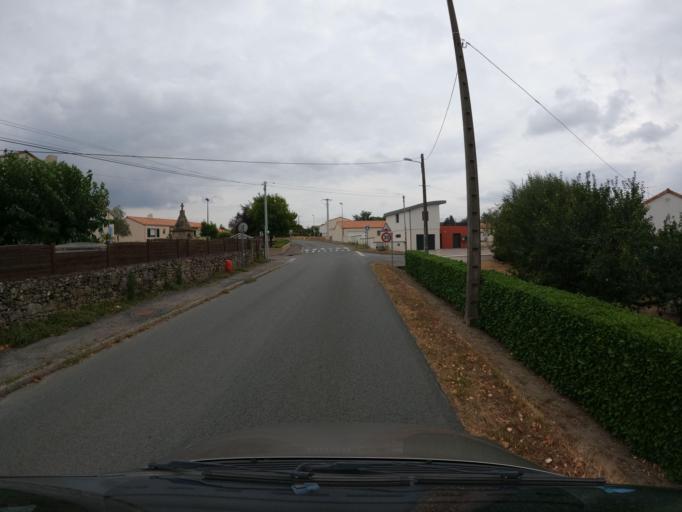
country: FR
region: Pays de la Loire
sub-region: Departement de la Vendee
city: Tiffauges
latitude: 47.0091
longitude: -1.1148
